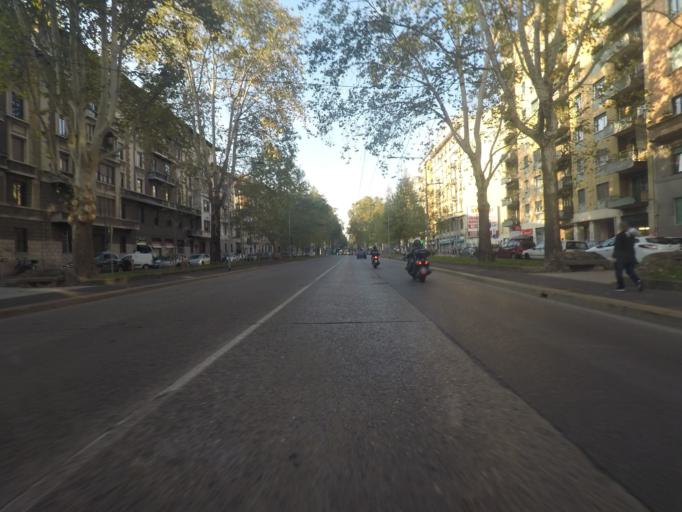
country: IT
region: Lombardy
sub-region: Citta metropolitana di Milano
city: Milano
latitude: 45.4745
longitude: 9.2238
